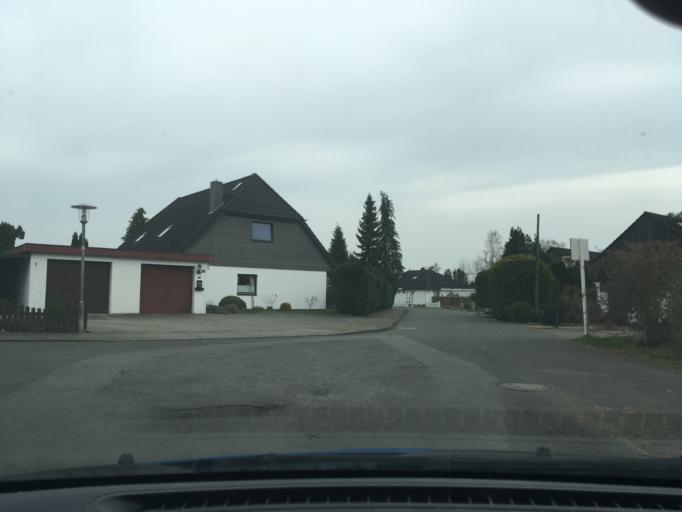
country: DE
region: Lower Saxony
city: Tespe
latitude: 53.3929
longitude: 10.4200
